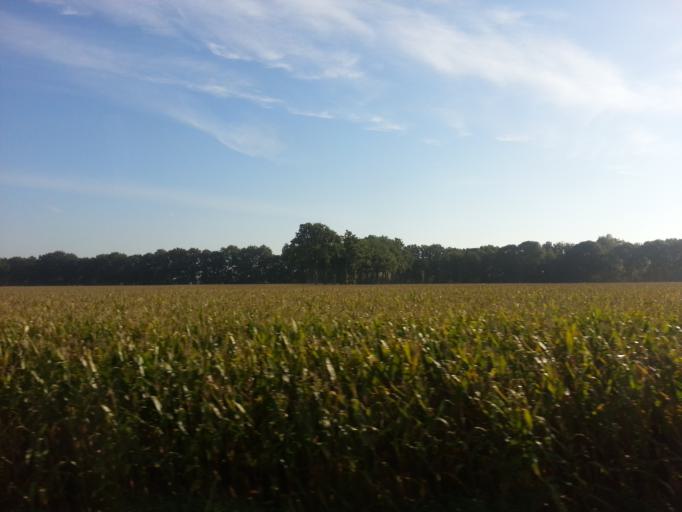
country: NL
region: North Brabant
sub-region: Gemeente Vught
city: Vught
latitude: 51.6289
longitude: 5.2966
